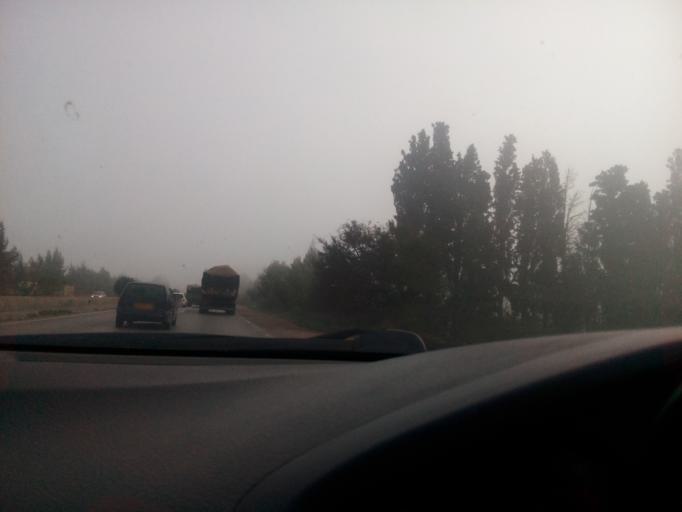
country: DZ
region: Oran
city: Bou Tlelis
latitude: 35.5907
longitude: -0.7988
